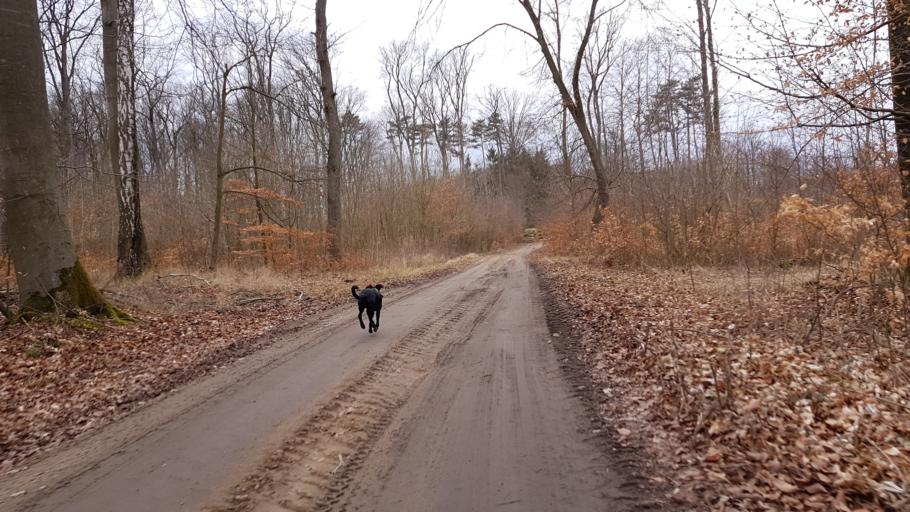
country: PL
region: West Pomeranian Voivodeship
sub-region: Powiat gryfinski
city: Banie
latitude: 53.0892
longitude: 14.7172
